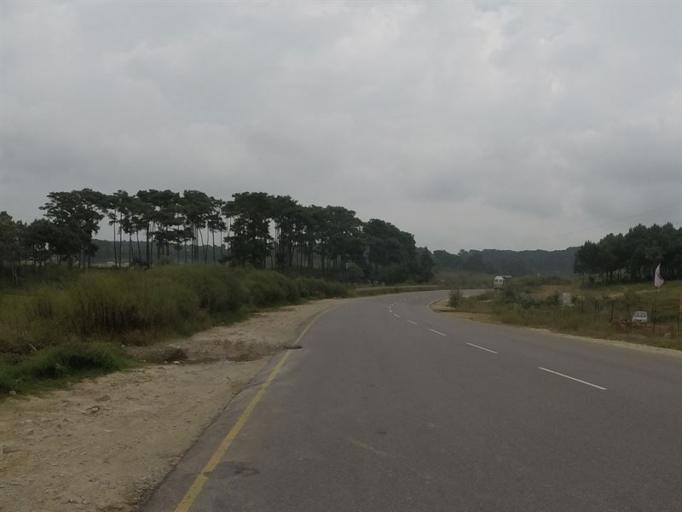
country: IN
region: Meghalaya
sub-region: East Khasi Hills
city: Shillong
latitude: 25.4952
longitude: 92.1728
